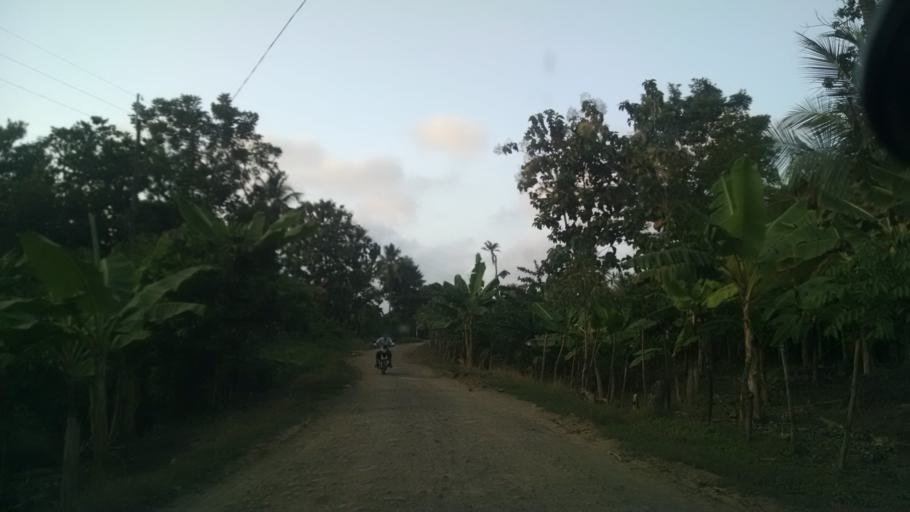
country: CO
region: Antioquia
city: San Juan de Uraba
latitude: 8.7248
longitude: -76.6045
